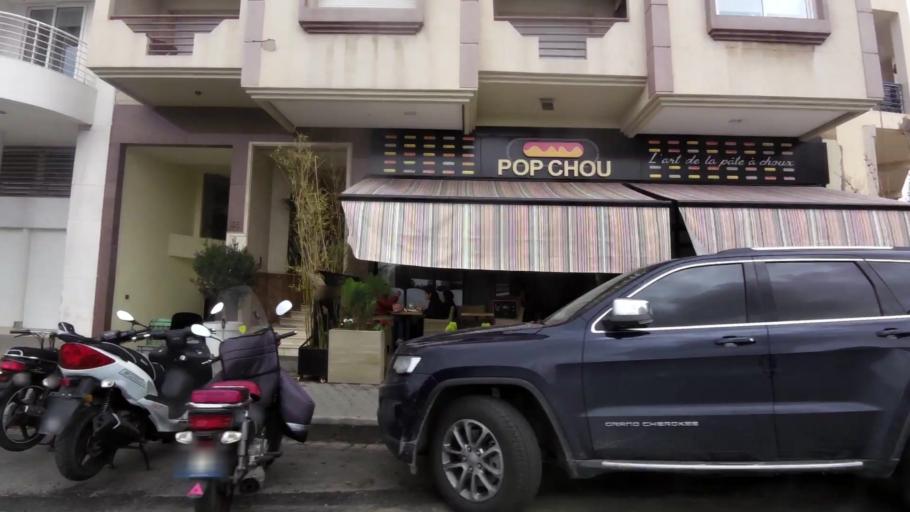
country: MA
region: Grand Casablanca
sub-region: Casablanca
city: Casablanca
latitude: 33.5943
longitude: -7.6447
